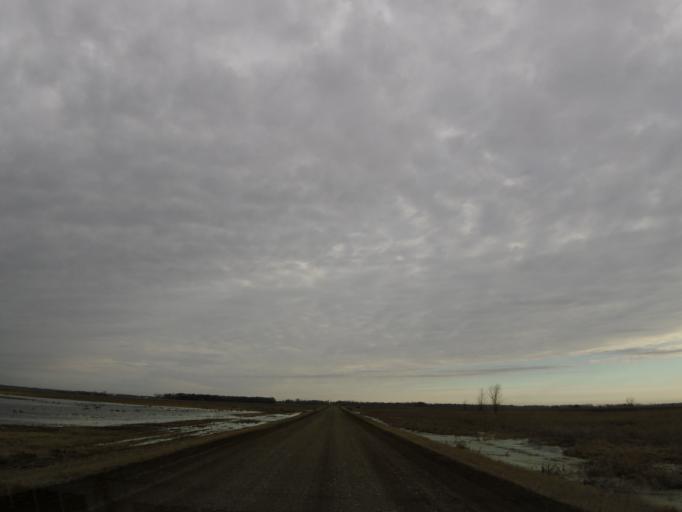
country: US
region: North Dakota
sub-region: Walsh County
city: Grafton
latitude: 48.4101
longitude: -97.4700
